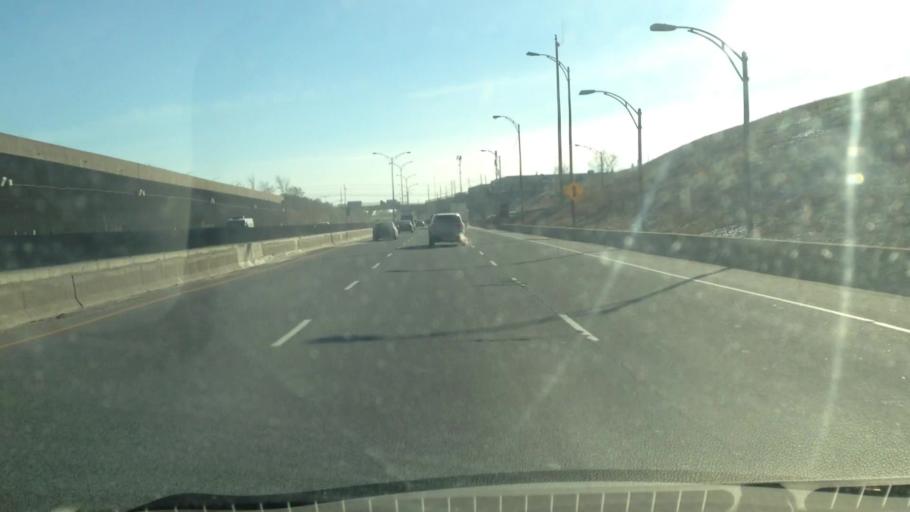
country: CA
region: Quebec
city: Cote-Saint-Luc
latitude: 45.4770
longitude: -73.7129
